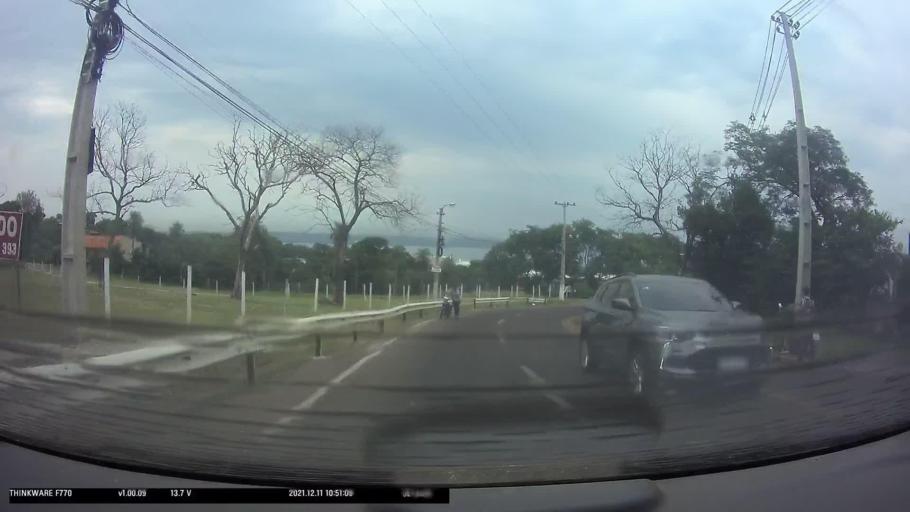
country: PY
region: Cordillera
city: San Bernardino
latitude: -25.2987
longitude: -57.2717
